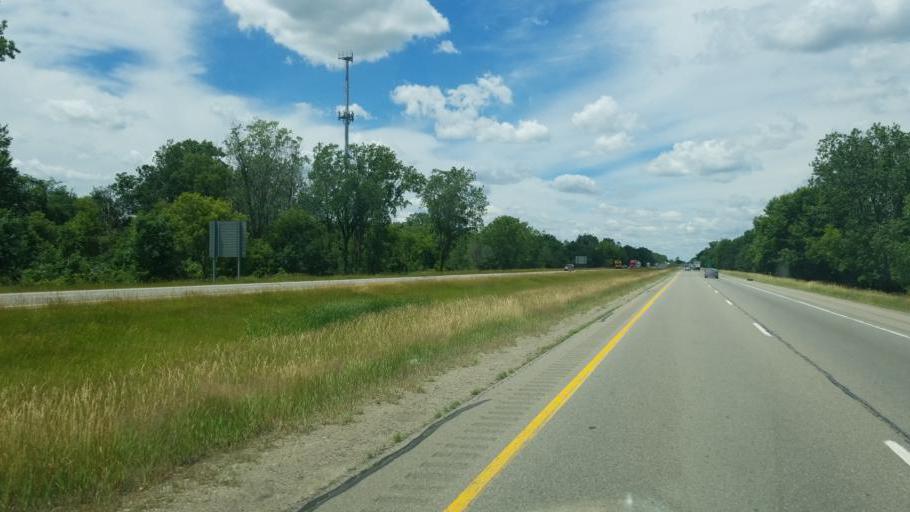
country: US
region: Michigan
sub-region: Ingham County
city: Holt
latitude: 42.6591
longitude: -84.5508
